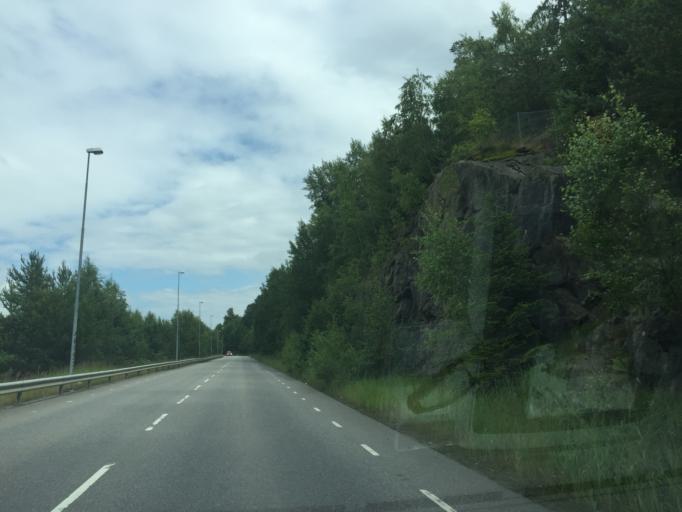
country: SE
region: Stockholm
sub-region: Botkyrka Kommun
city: Tumba
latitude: 59.1986
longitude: 17.8644
